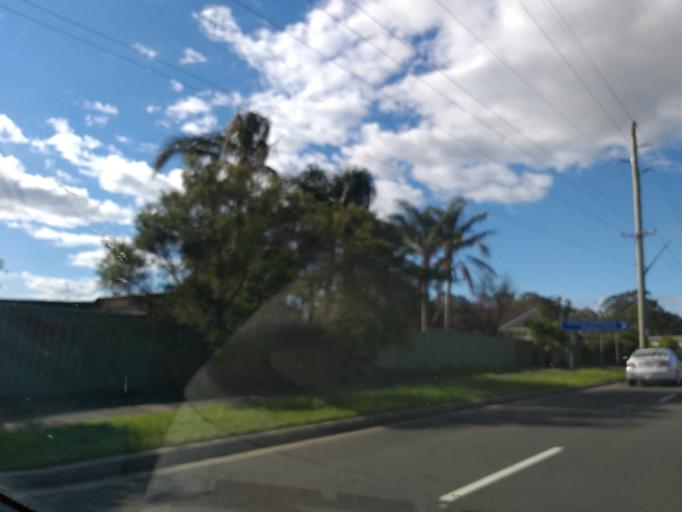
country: AU
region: New South Wales
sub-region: Shellharbour
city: Barrack Heights
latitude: -34.5625
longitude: 150.8348
